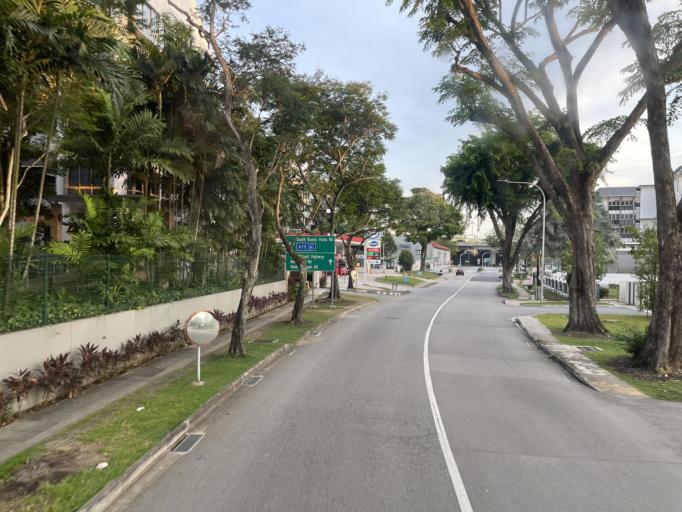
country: SG
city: Singapore
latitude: 1.2807
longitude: 103.7851
